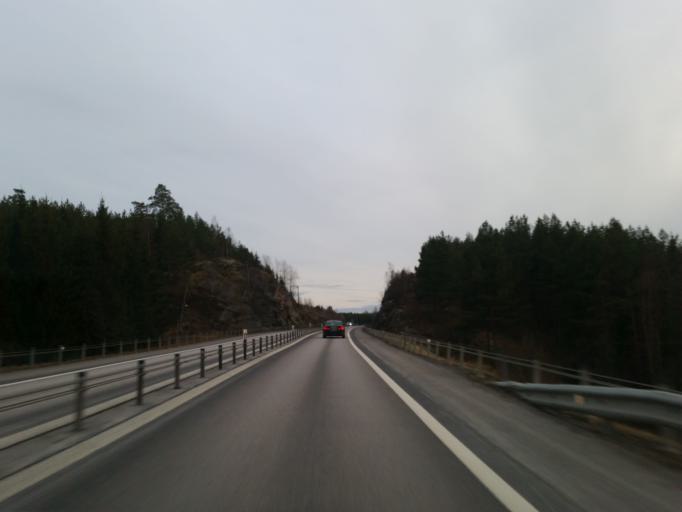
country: SE
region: OEstergoetland
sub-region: Valdemarsviks Kommun
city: Gusum
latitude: 58.2737
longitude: 16.5164
